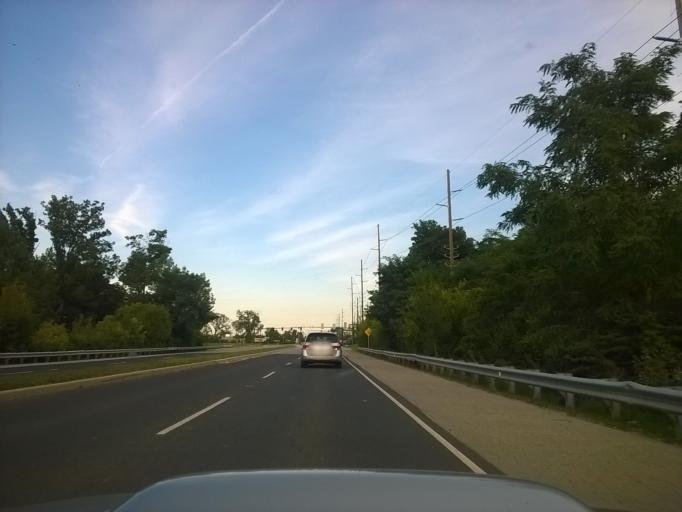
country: US
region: Indiana
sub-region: Hamilton County
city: Fishers
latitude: 39.9269
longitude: -86.0735
